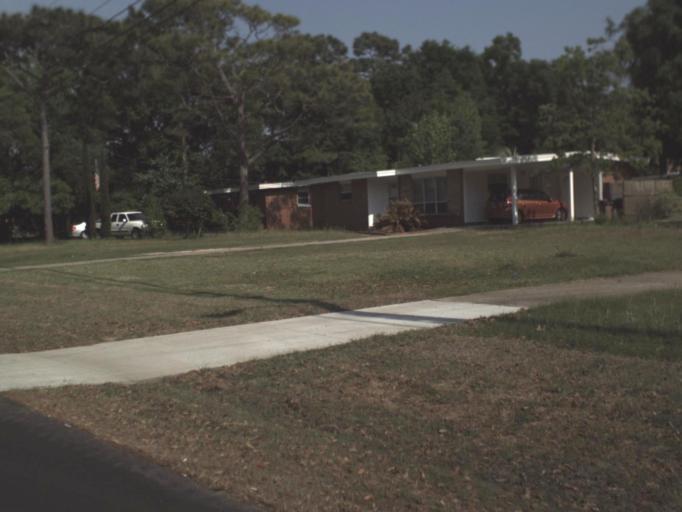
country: US
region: Florida
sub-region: Escambia County
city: Ferry Pass
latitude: 30.4998
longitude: -87.1778
